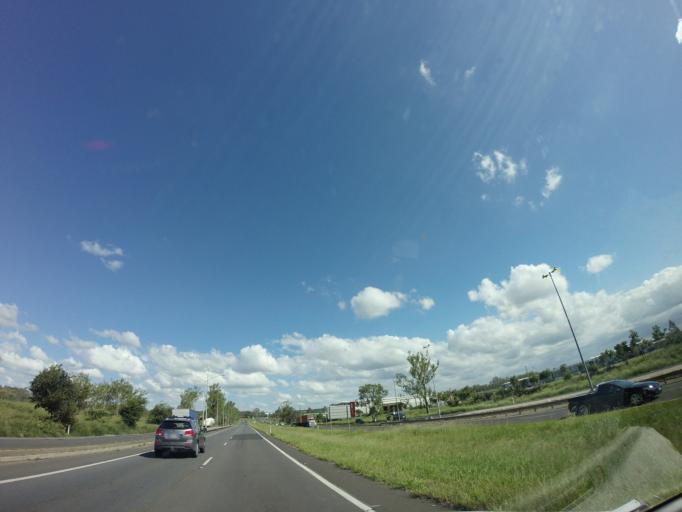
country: AU
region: Queensland
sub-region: Ipswich
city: Bundamba
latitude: -27.5855
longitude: 152.8195
